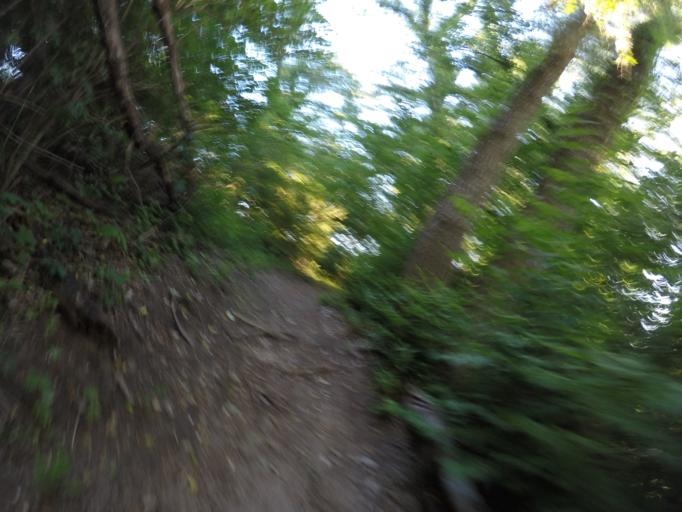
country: US
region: Kansas
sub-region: Riley County
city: Manhattan
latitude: 39.1839
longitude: -96.5441
